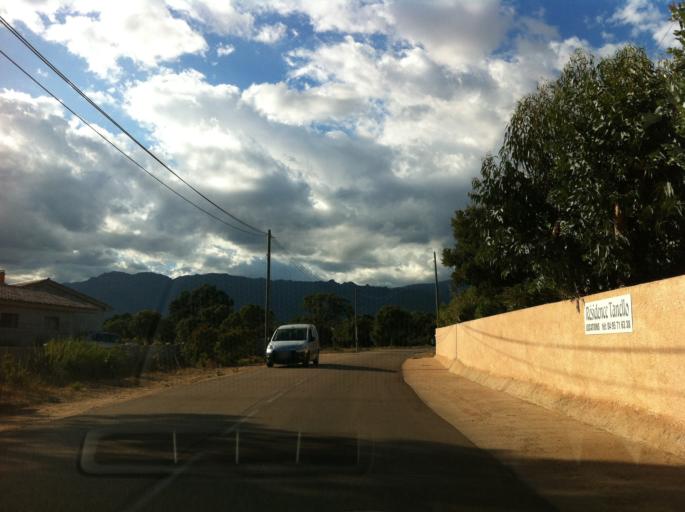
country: FR
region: Corsica
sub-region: Departement de la Corse-du-Sud
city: Porto-Vecchio
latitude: 41.6430
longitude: 9.3307
